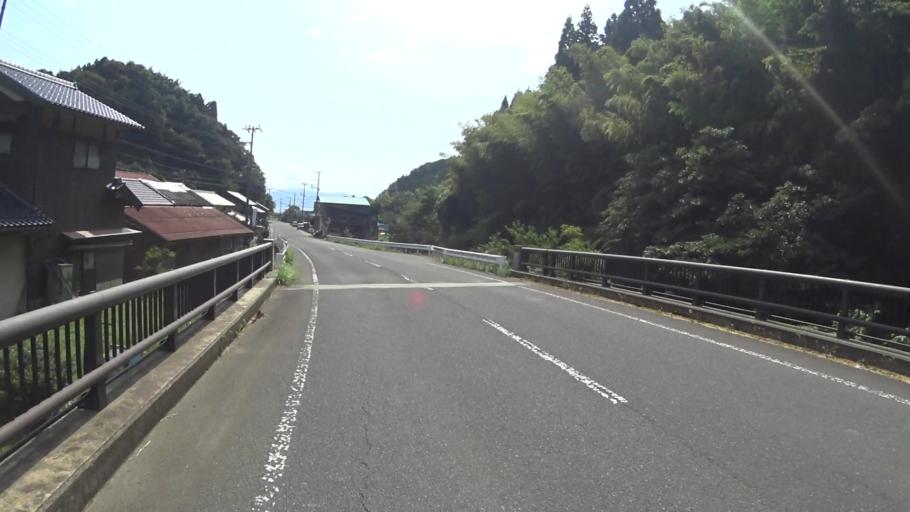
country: JP
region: Kyoto
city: Miyazu
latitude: 35.6612
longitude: 135.2532
